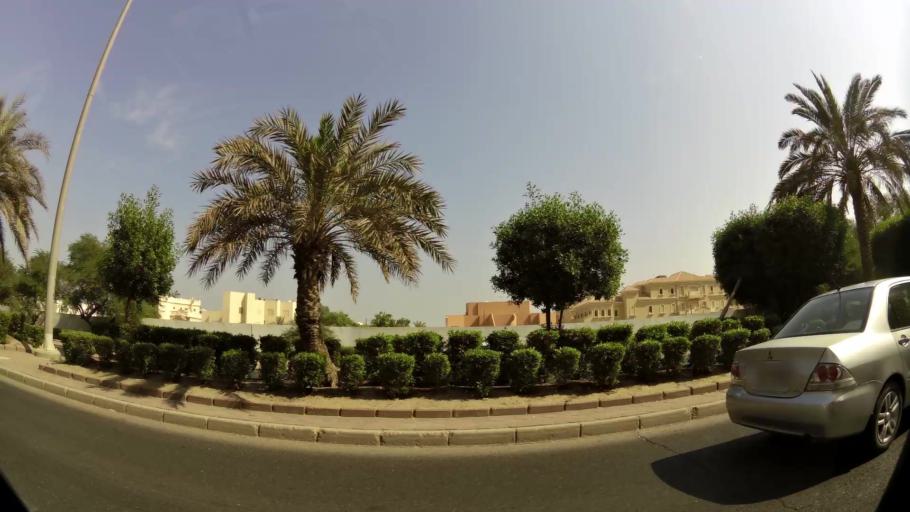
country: KW
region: Al Ahmadi
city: Al Mahbulah
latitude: 29.1522
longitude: 48.1253
